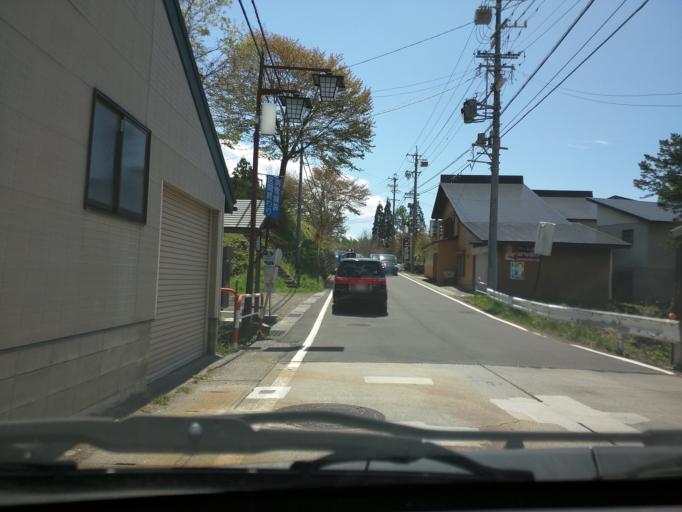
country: JP
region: Nagano
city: Nagano-shi
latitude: 36.7282
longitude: 138.0774
